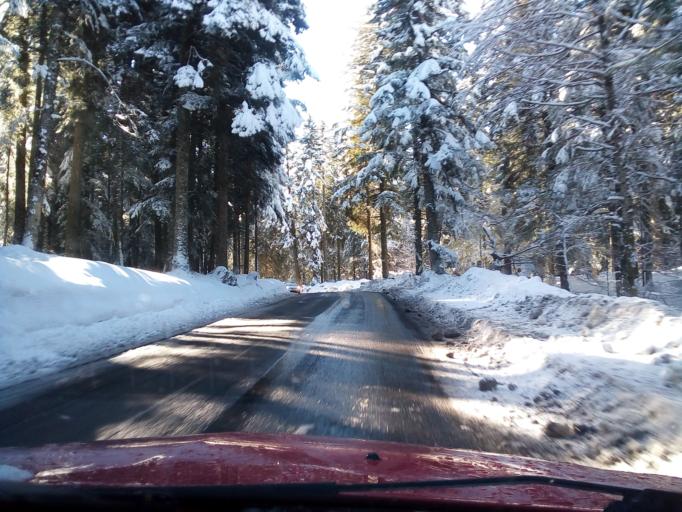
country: FR
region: Rhone-Alpes
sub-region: Departement de l'Isere
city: Le Sappey-en-Chartreuse
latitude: 45.3048
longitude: 5.7684
